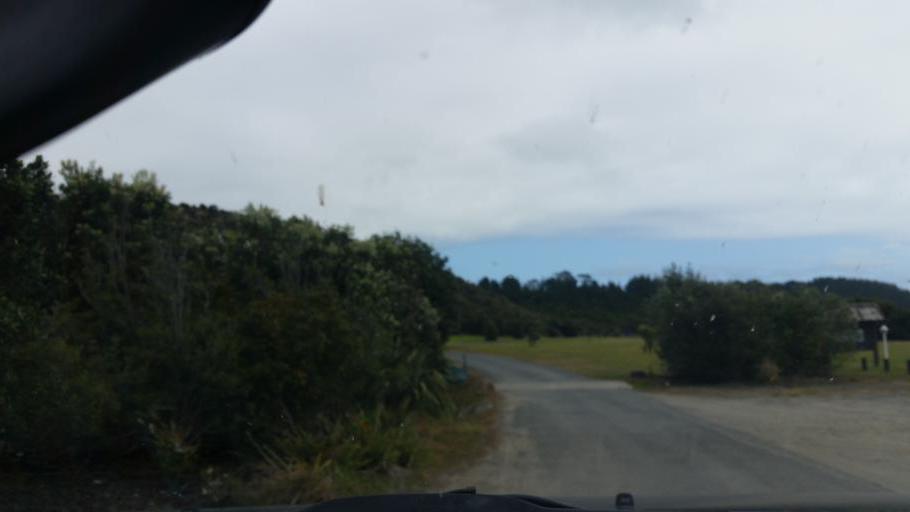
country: NZ
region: Northland
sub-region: Kaipara District
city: Dargaville
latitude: -35.8092
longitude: 173.6627
